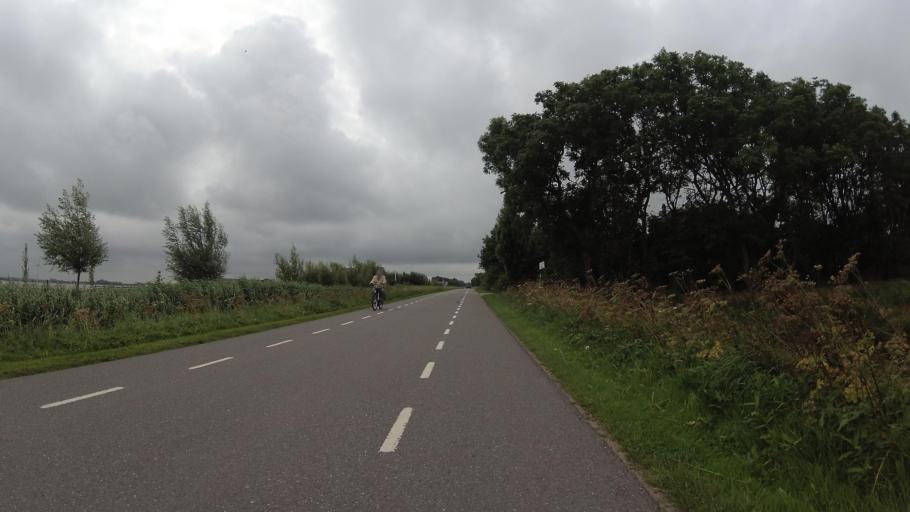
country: NL
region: North Holland
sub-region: Gemeente Den Helder
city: Den Helder
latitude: 52.8761
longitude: 4.7491
